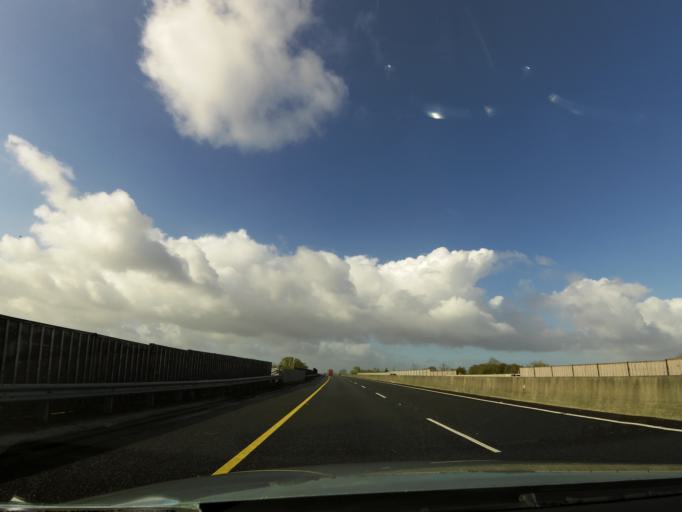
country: IE
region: Munster
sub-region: County Limerick
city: Castleconnell
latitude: 52.7118
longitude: -8.4784
